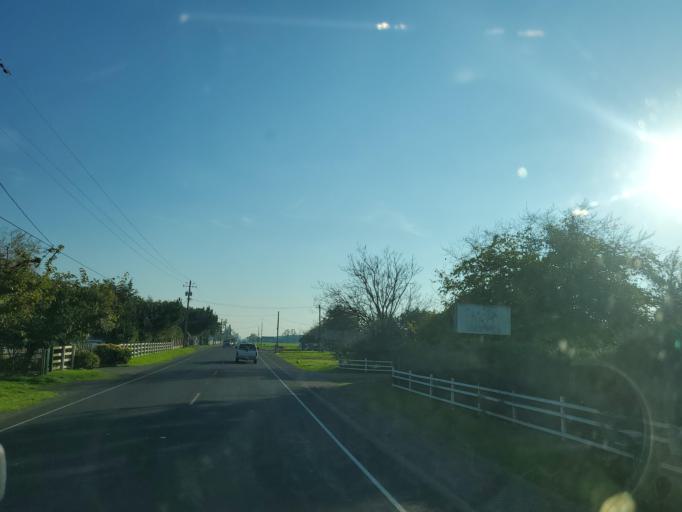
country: US
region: California
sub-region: San Joaquin County
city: French Camp
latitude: 37.8638
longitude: -121.2559
